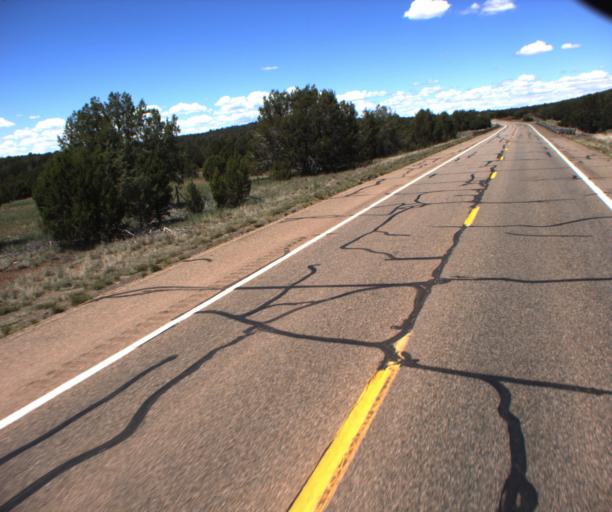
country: US
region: Arizona
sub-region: Yavapai County
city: Paulden
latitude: 35.1225
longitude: -112.4351
